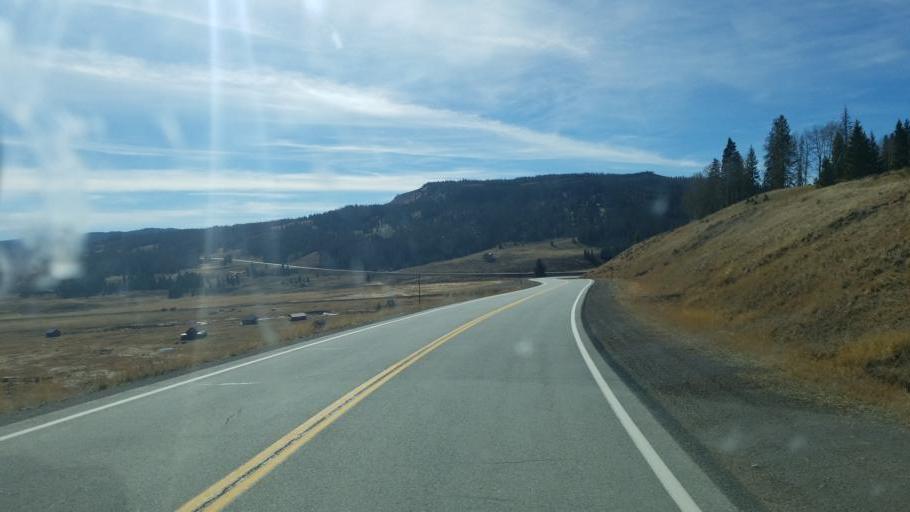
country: US
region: New Mexico
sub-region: Rio Arriba County
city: Chama
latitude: 37.0478
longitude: -106.4013
